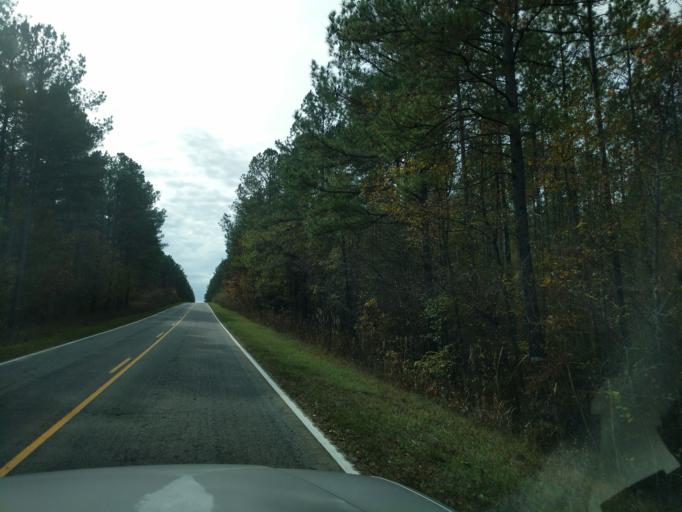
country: US
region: South Carolina
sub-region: Greenwood County
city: Ninety Six
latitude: 34.2254
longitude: -81.8773
